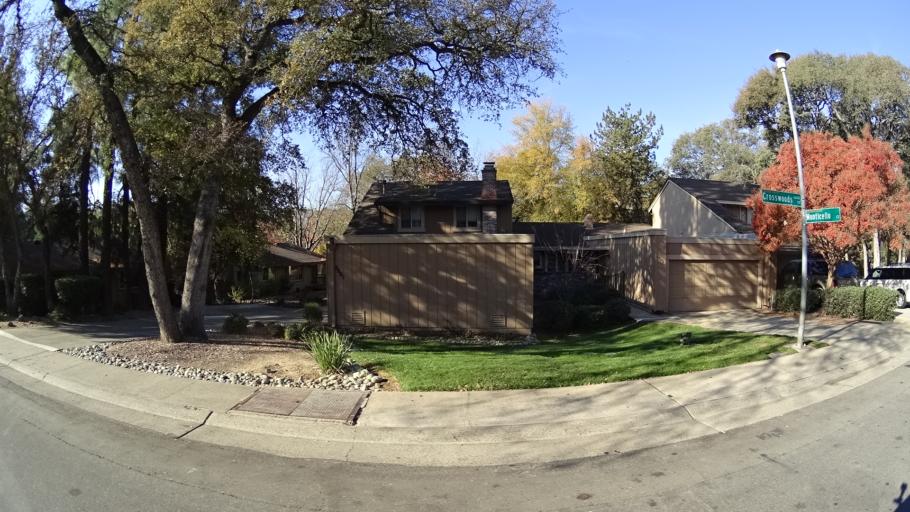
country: US
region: California
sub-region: Sacramento County
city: Citrus Heights
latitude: 38.6860
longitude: -121.3046
